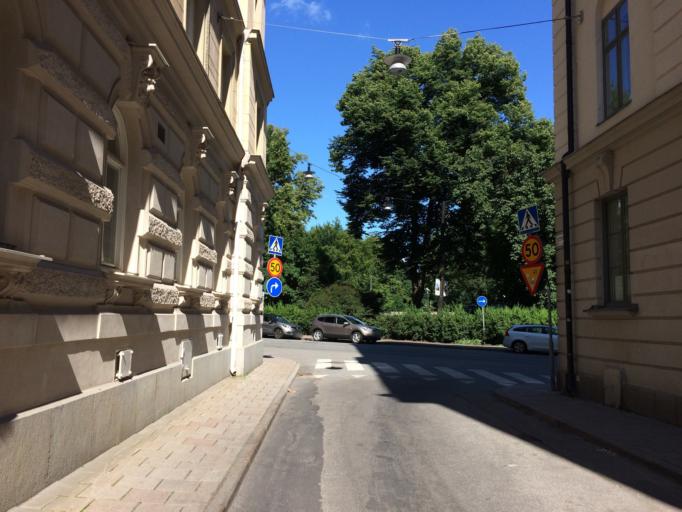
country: SE
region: Stockholm
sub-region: Stockholms Kommun
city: Stockholm
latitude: 59.3398
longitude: 18.0695
